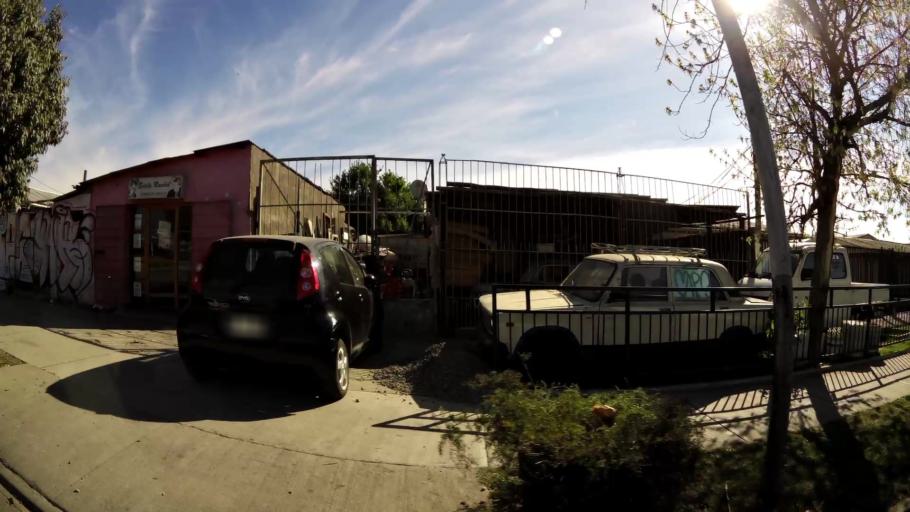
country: CL
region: Santiago Metropolitan
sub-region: Provincia de Santiago
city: Santiago
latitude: -33.5126
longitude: -70.6252
